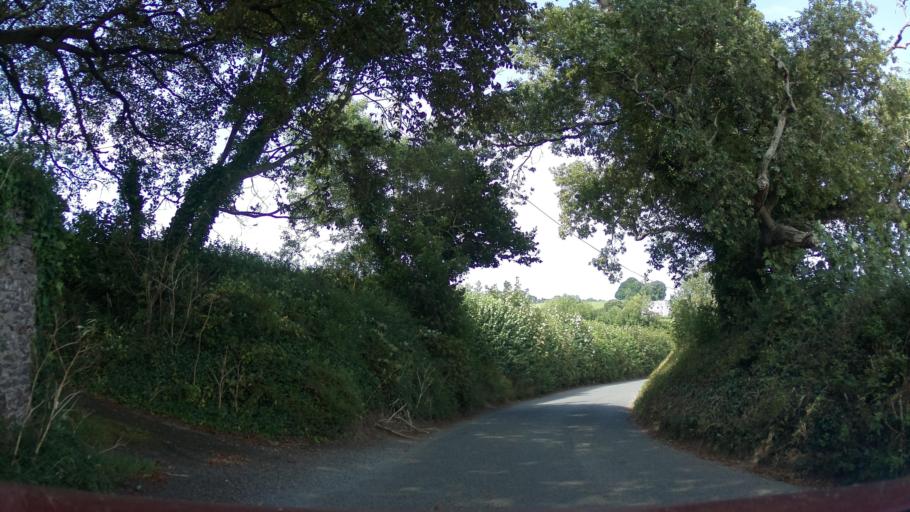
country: GB
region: England
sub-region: Borough of Torbay
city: Paignton
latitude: 50.4001
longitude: -3.6043
